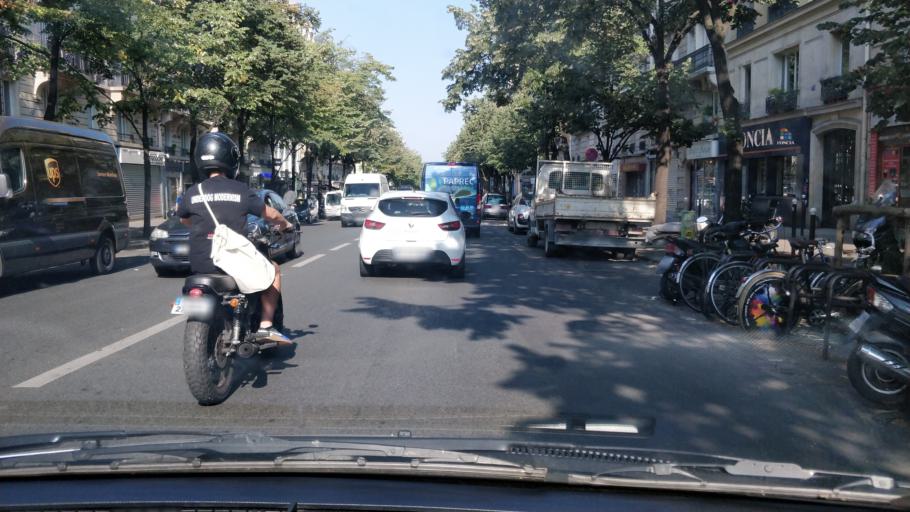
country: FR
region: Ile-de-France
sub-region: Departement de Seine-Saint-Denis
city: Le Pre-Saint-Gervais
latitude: 48.8643
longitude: 2.3803
